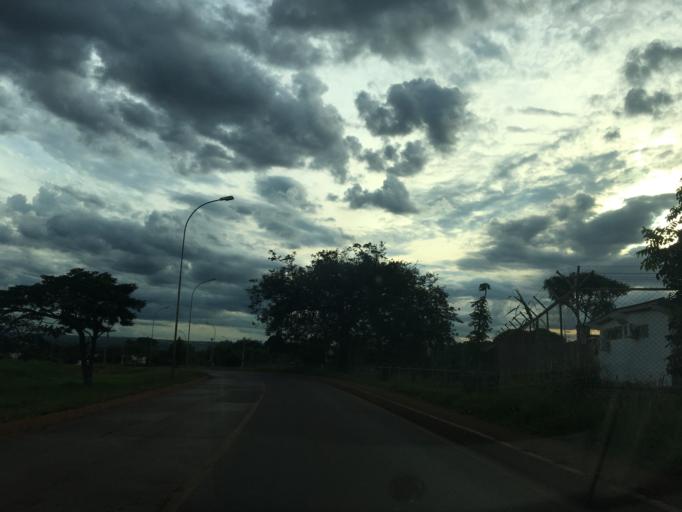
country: BR
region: Federal District
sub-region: Brasilia
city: Brasilia
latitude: -15.8320
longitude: -47.9315
